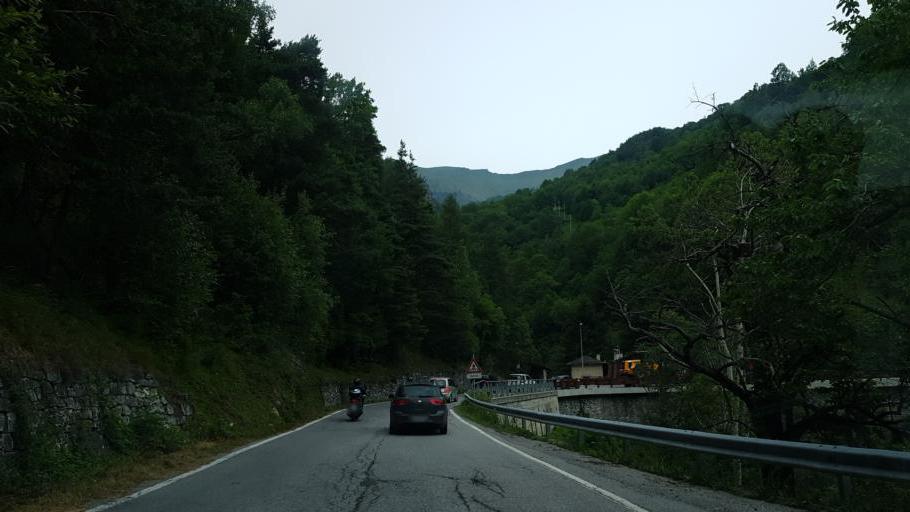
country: IT
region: Piedmont
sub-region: Provincia di Cuneo
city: Stroppo
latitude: 44.5031
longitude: 7.1223
